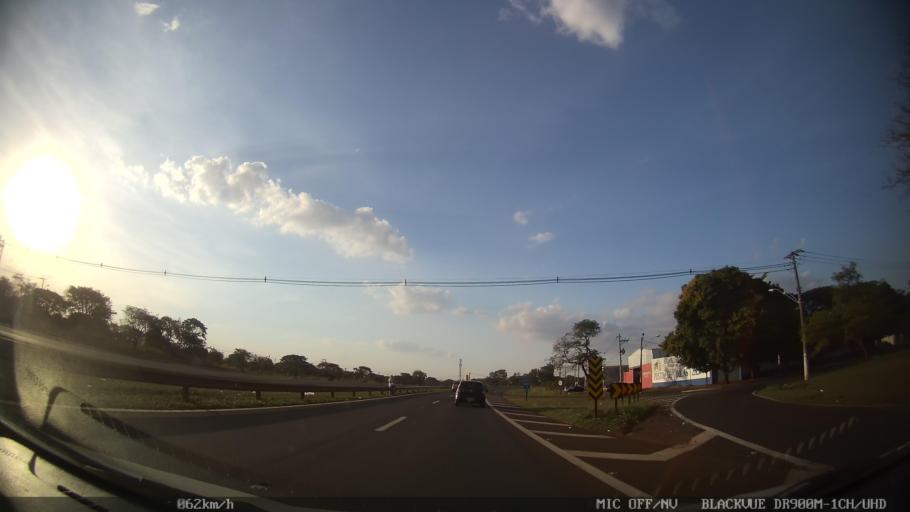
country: BR
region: Sao Paulo
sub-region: Ribeirao Preto
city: Ribeirao Preto
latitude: -21.1214
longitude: -47.7861
